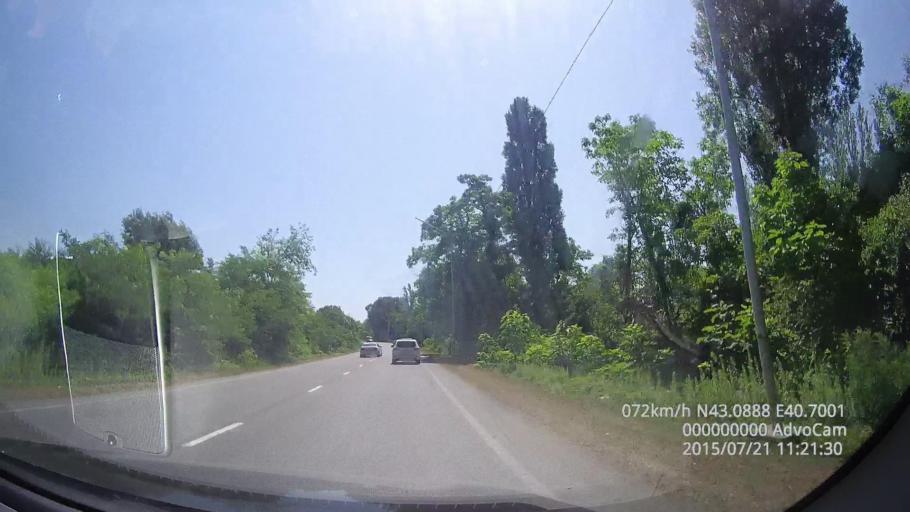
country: GE
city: P'rimorsk'oe
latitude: 43.0887
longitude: 40.7006
